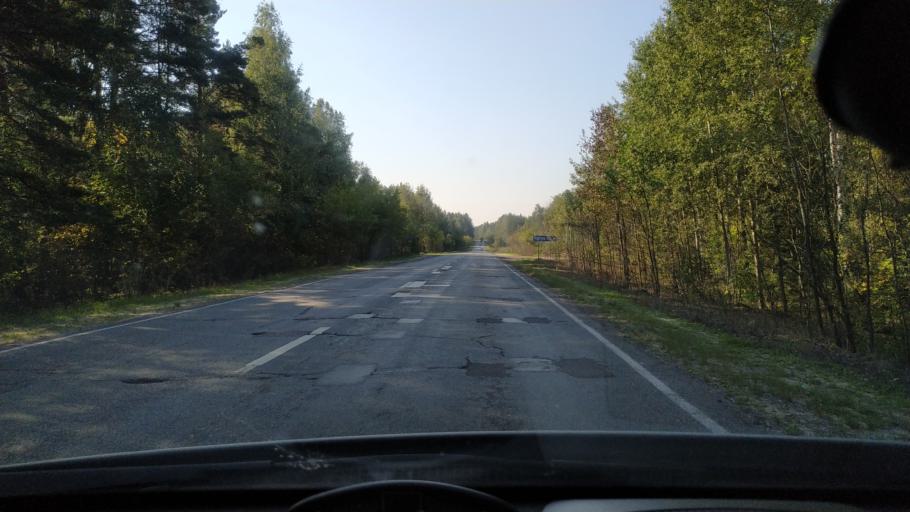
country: RU
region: Moskovskaya
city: Tugolesskiy Bor
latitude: 55.5469
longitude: 39.7041
